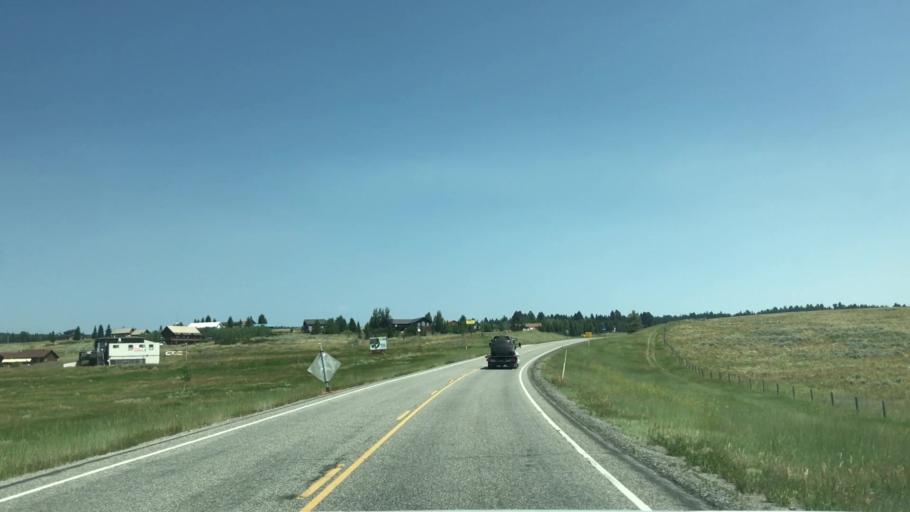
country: US
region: Montana
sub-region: Gallatin County
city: West Yellowstone
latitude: 44.7882
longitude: -111.1125
